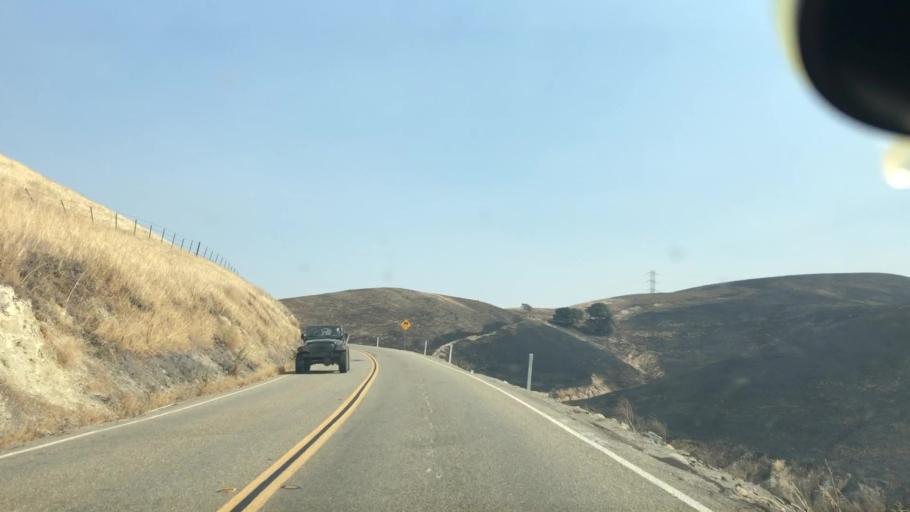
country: US
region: California
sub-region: San Joaquin County
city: Mountain House
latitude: 37.6505
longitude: -121.6128
